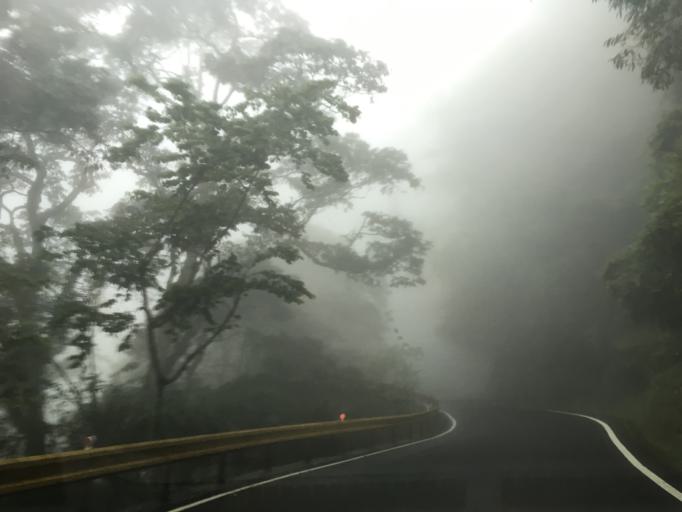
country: TW
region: Taiwan
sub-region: Hualien
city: Hualian
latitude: 24.1950
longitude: 121.4220
